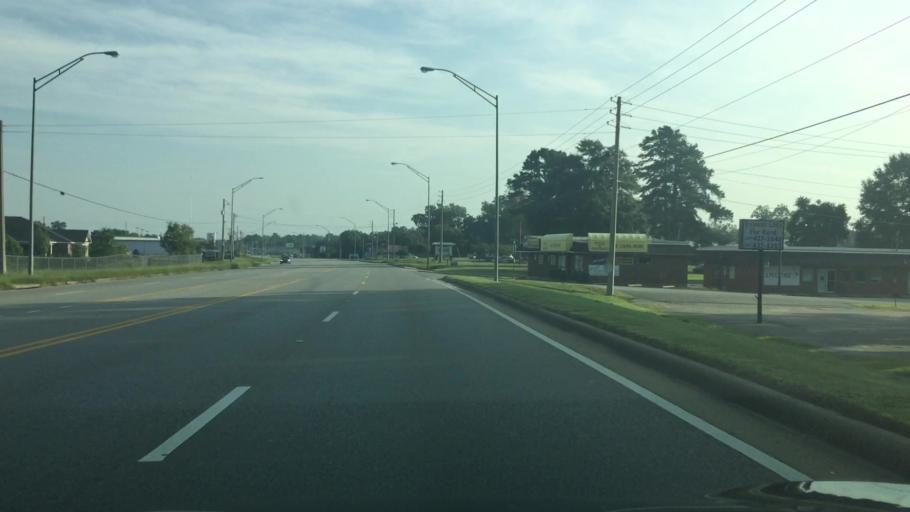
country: US
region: Alabama
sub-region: Covington County
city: Andalusia
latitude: 31.2995
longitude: -86.4994
